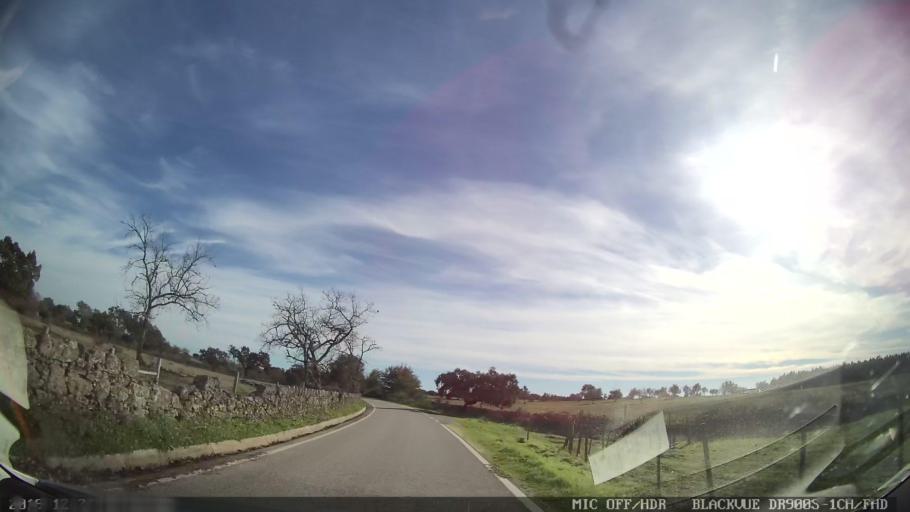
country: PT
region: Portalegre
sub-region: Nisa
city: Nisa
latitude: 39.4884
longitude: -7.7399
